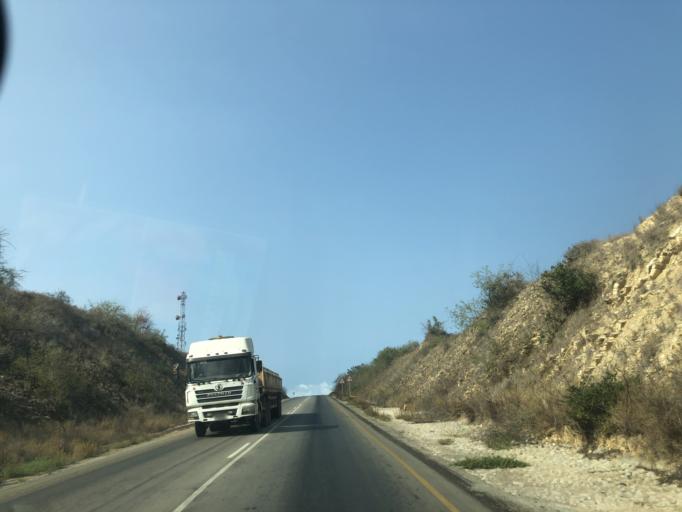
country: AO
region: Luanda
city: Luanda
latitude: -9.6912
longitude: 13.2136
